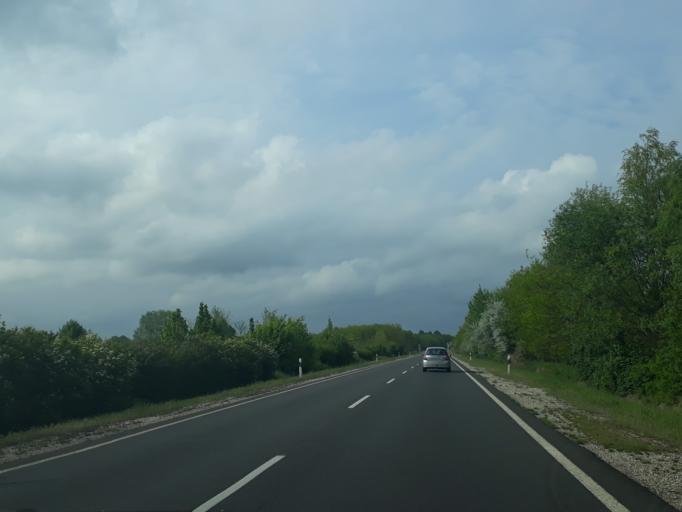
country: HU
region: Szabolcs-Szatmar-Bereg
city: Nyirtass
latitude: 48.0936
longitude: 21.9872
